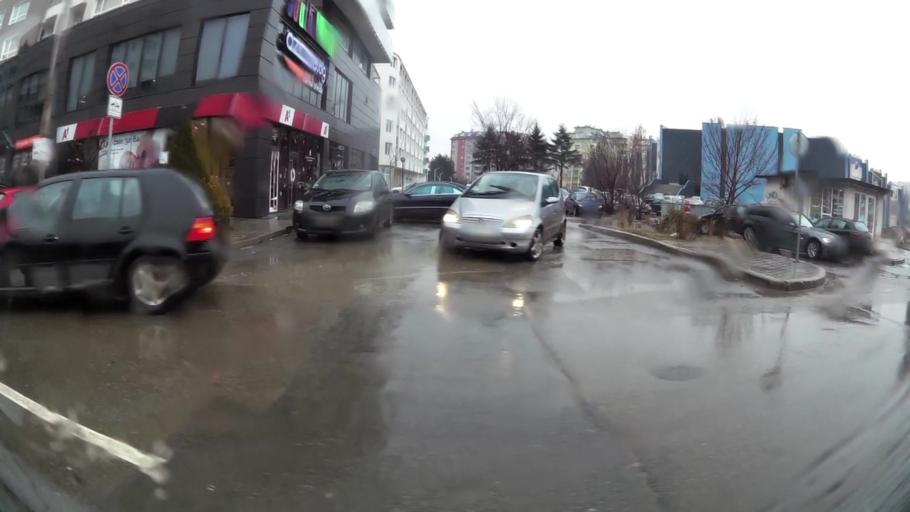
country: BG
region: Sofia-Capital
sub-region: Stolichna Obshtina
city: Sofia
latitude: 42.6448
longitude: 23.3421
